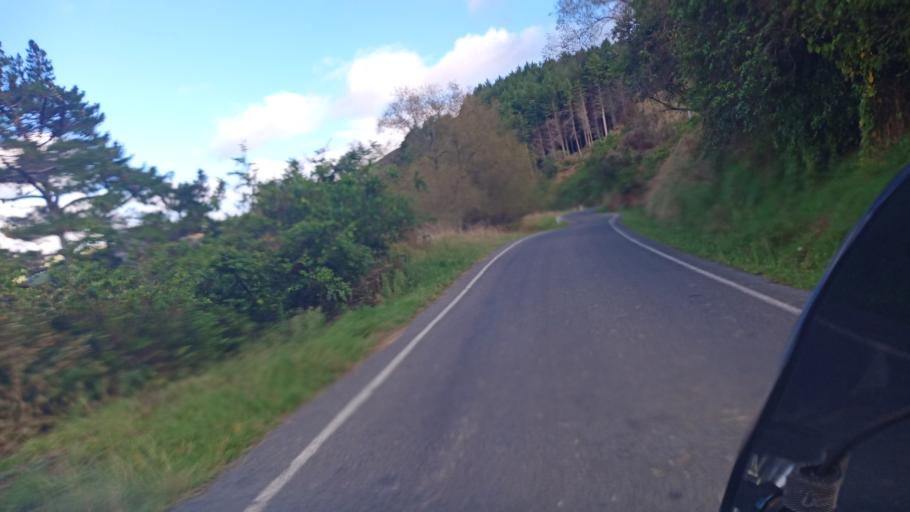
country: NZ
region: Gisborne
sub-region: Gisborne District
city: Gisborne
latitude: -38.5310
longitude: 177.5492
